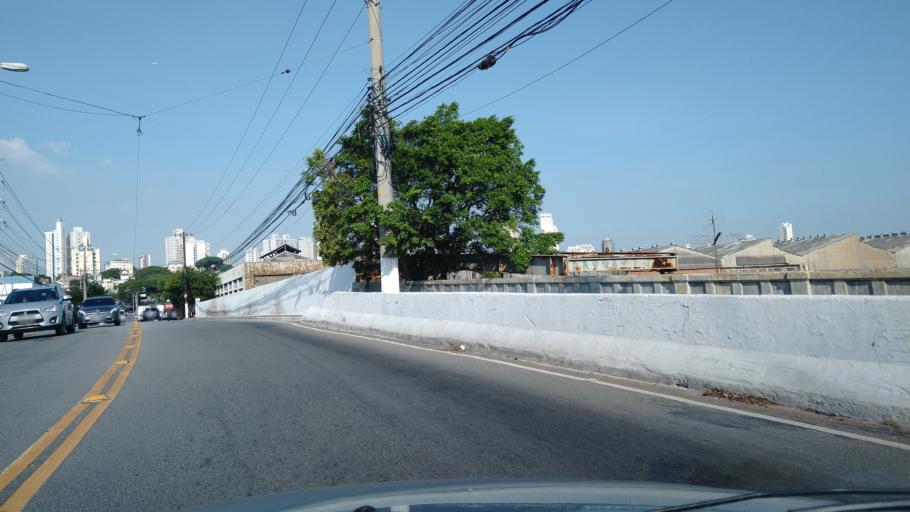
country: BR
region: Sao Paulo
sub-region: Sao Paulo
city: Sao Paulo
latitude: -23.5674
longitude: -46.6045
